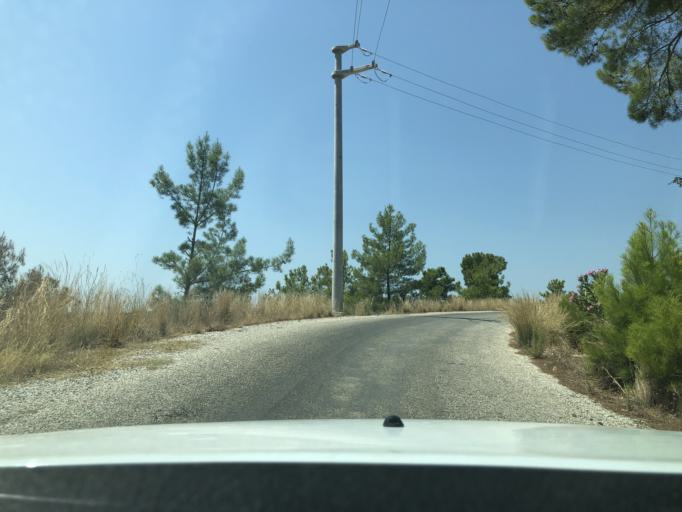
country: TR
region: Antalya
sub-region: Manavgat
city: Kizilagac
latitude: 36.8678
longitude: 31.5577
